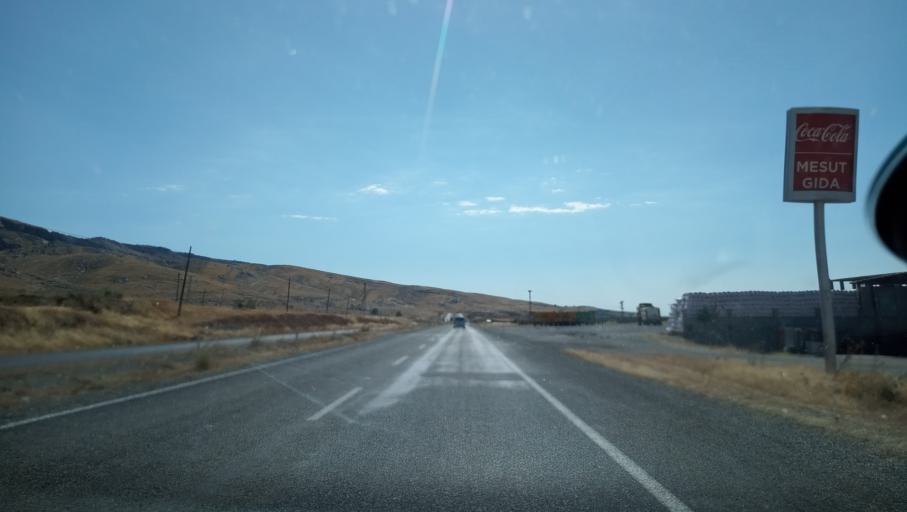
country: TR
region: Diyarbakir
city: Silvan
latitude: 38.1279
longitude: 41.0727
